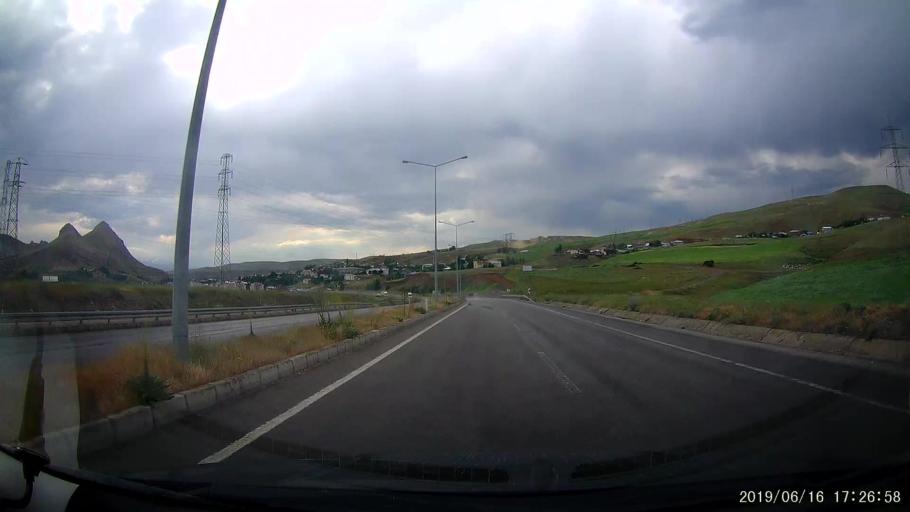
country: TR
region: Erzincan
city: Tercan
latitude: 39.7734
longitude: 40.4019
